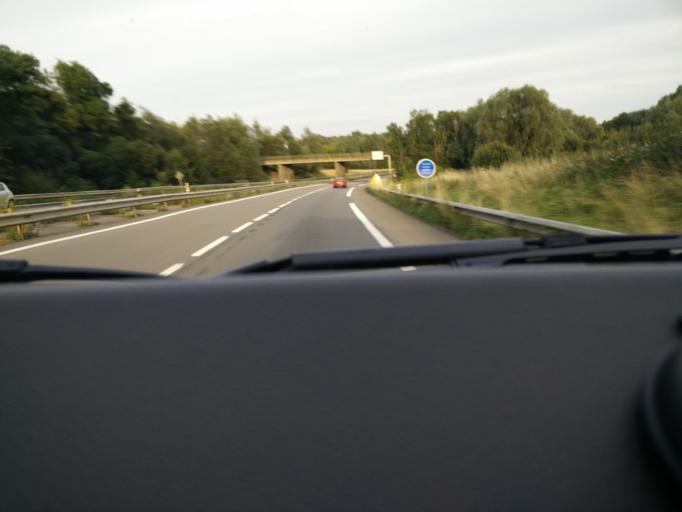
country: FR
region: Nord-Pas-de-Calais
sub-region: Departement du Nord
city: Curgies
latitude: 50.3291
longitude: 3.5905
